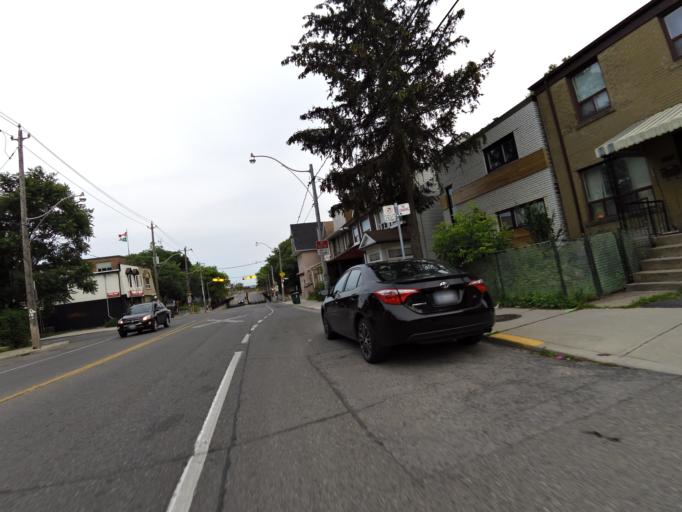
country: CA
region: Ontario
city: Toronto
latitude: 43.6732
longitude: -79.3374
